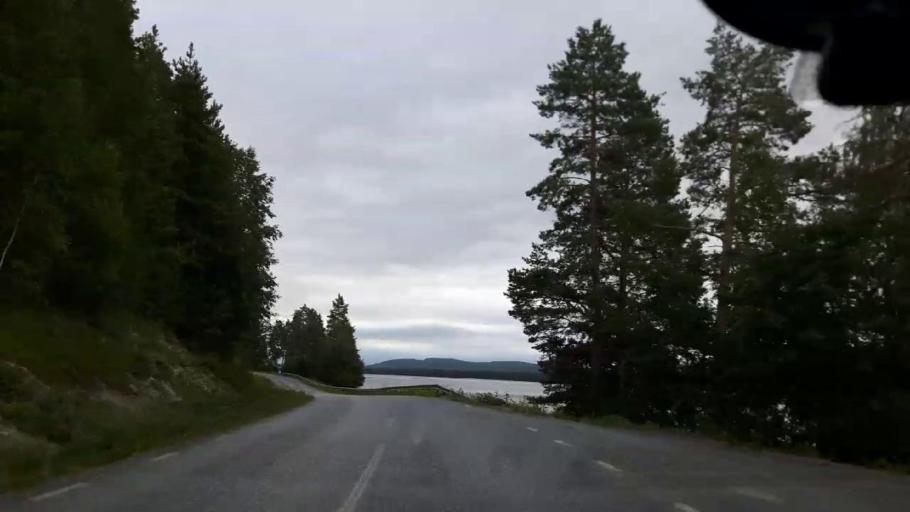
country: SE
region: Jaemtland
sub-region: Braecke Kommun
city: Braecke
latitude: 62.8649
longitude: 15.6186
